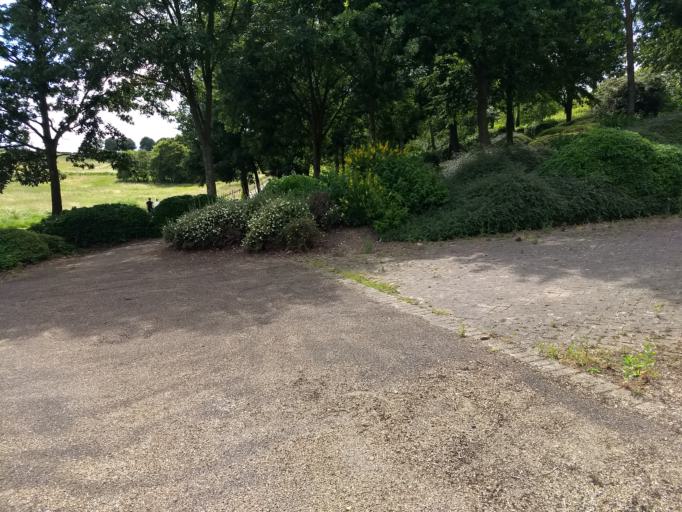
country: GB
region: England
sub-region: Milton Keynes
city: Milton Keynes
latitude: 52.0488
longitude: -0.7438
